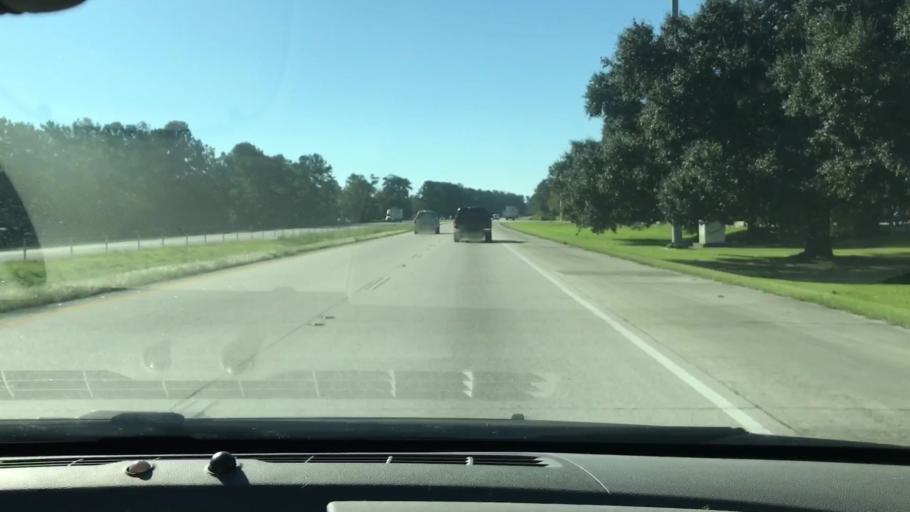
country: US
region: Louisiana
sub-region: Saint Tammany Parish
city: Pearl River
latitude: 30.3223
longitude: -89.7378
